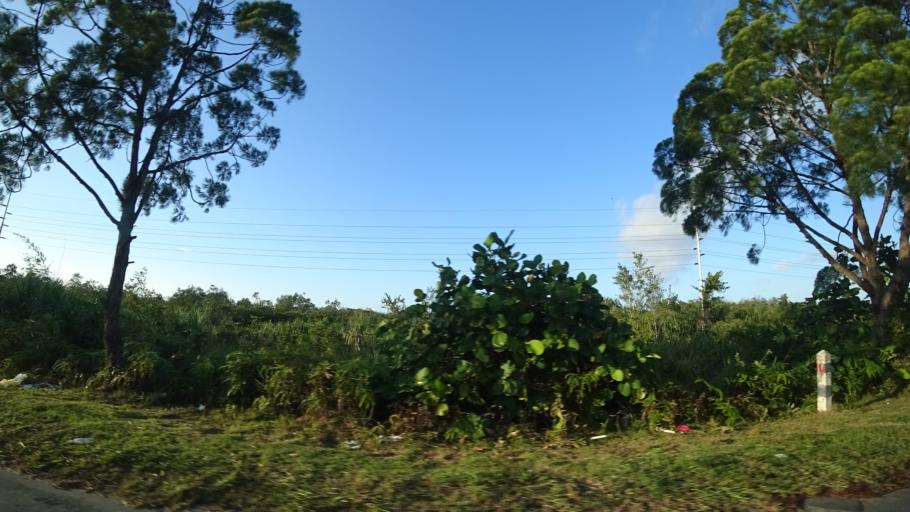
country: BN
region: Tutong
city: Tutong
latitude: 4.7329
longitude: 114.5683
